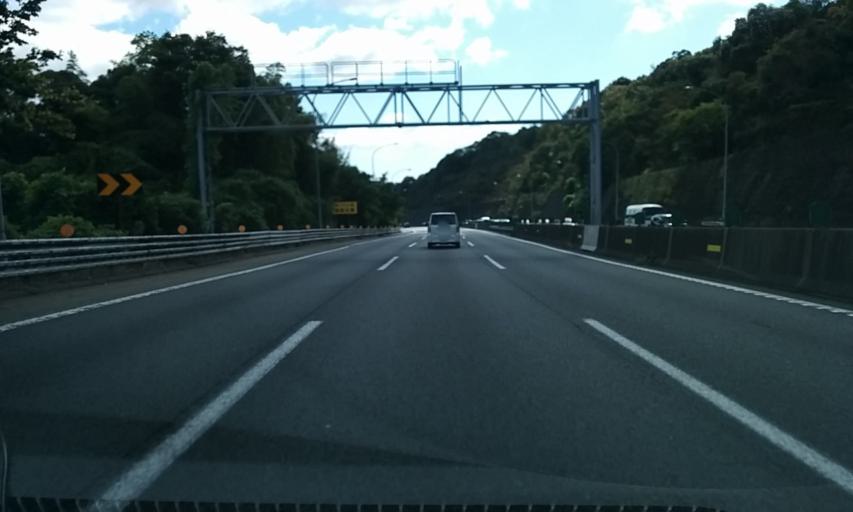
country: JP
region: Hyogo
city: Takarazuka
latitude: 34.8267
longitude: 135.3049
